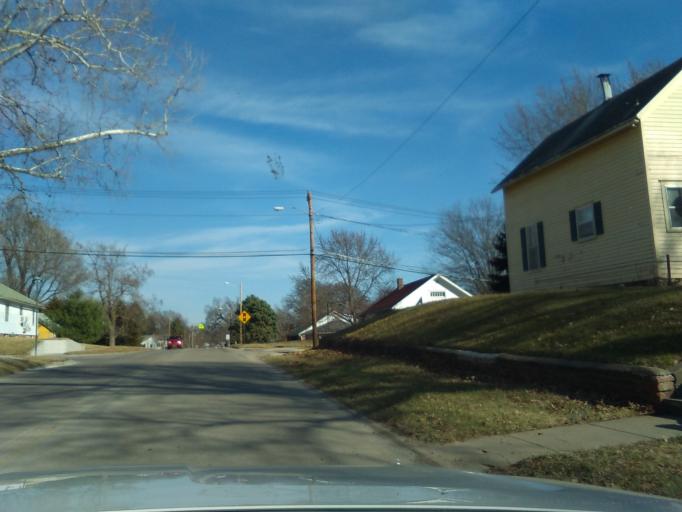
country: US
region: Nebraska
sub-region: Otoe County
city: Nebraska City
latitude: 40.6730
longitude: -95.8658
